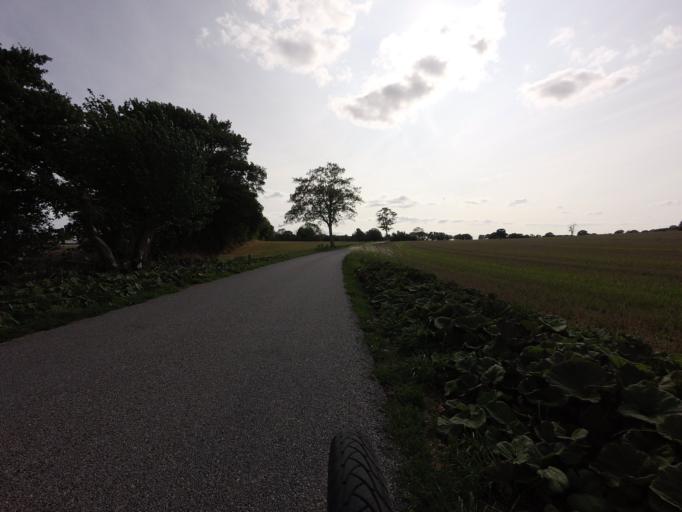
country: DK
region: Zealand
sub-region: Faxe Kommune
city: Fakse
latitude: 55.2054
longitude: 12.1123
